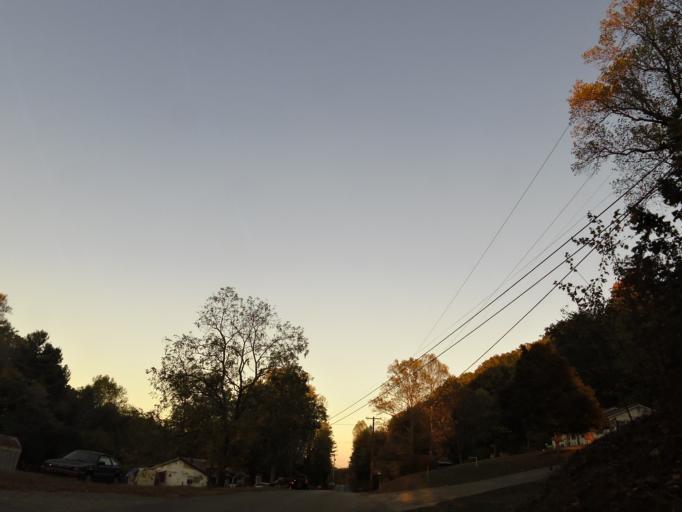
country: US
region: Tennessee
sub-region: Blount County
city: Eagleton Village
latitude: 35.8391
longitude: -83.9164
